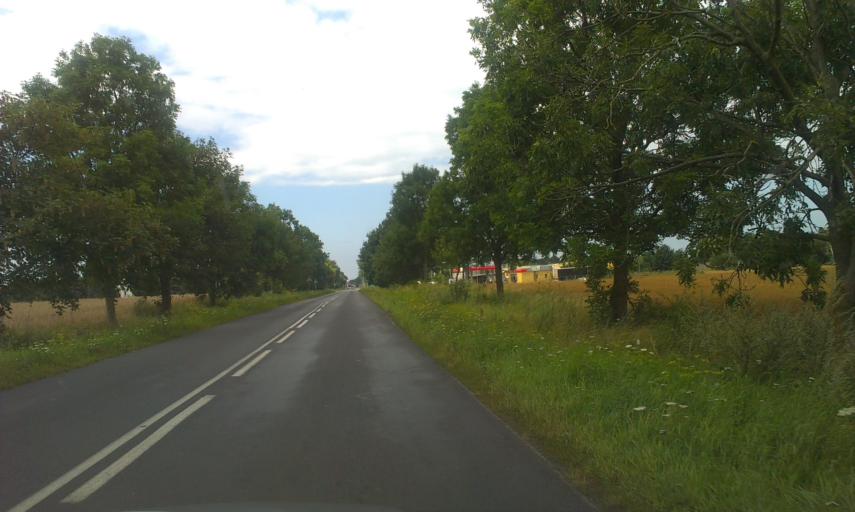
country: PL
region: West Pomeranian Voivodeship
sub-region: Powiat kolobrzeski
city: Dygowo
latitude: 54.1257
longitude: 15.7302
